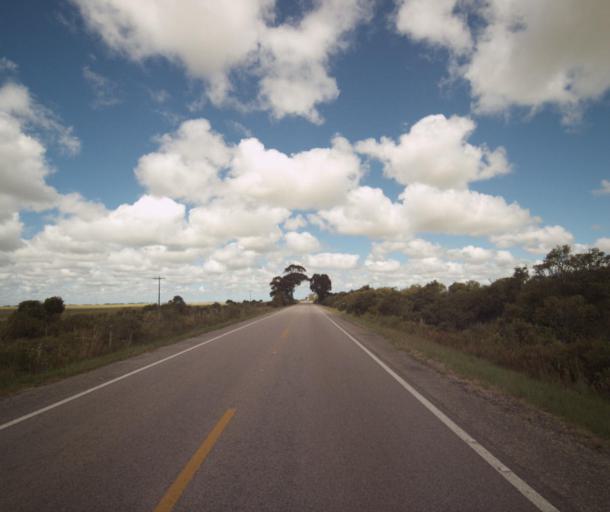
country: BR
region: Rio Grande do Sul
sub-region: Rio Grande
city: Rio Grande
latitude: -32.1870
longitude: -52.4298
